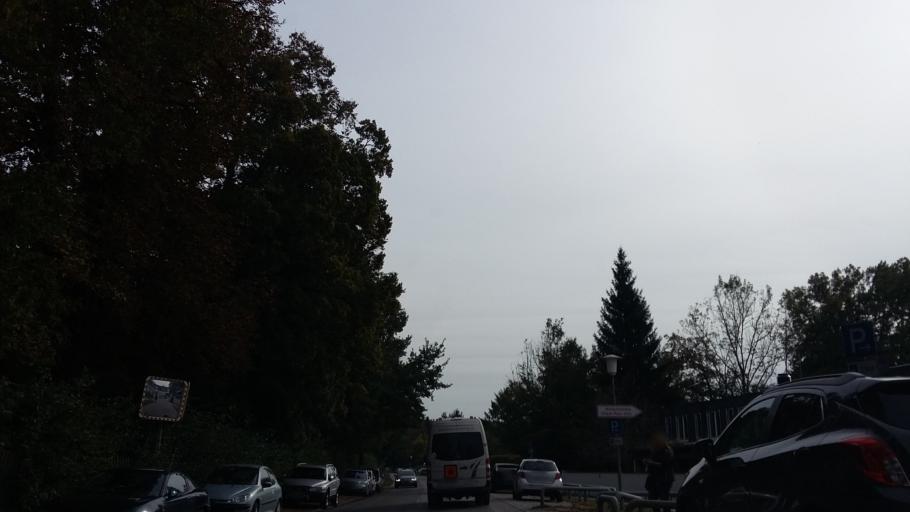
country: DE
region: Bavaria
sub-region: Upper Bavaria
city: Berg
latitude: 47.9874
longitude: 11.3615
